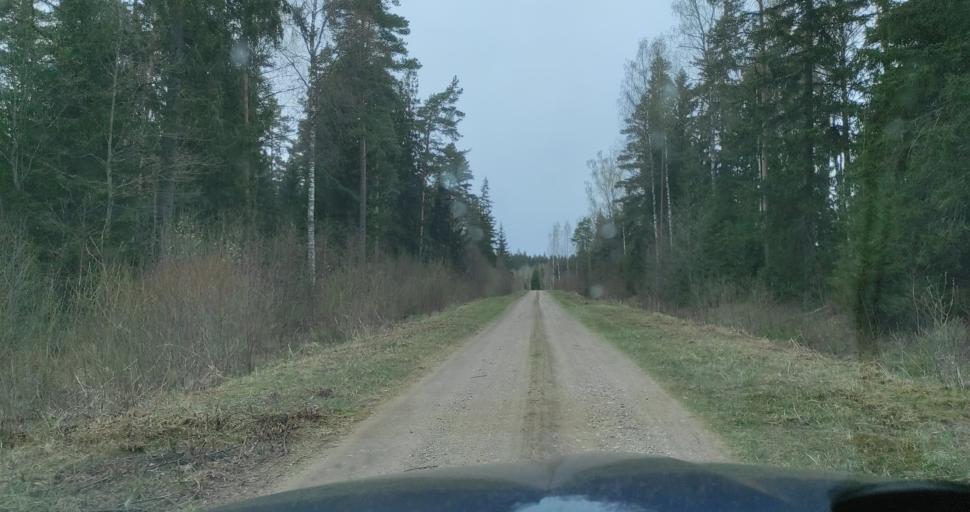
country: LV
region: Dundaga
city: Dundaga
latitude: 57.3598
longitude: 22.1518
